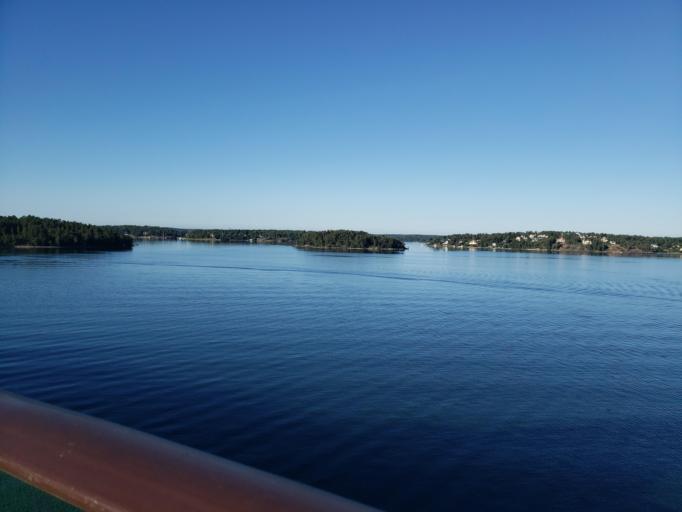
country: SE
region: Stockholm
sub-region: Vaxholms Kommun
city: Vaxholm
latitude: 59.4338
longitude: 18.3834
